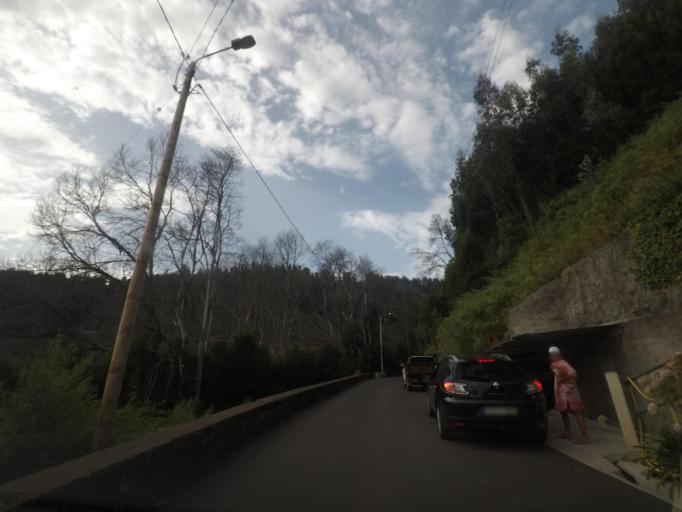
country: PT
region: Madeira
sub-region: Calheta
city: Arco da Calheta
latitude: 32.7412
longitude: -17.1533
